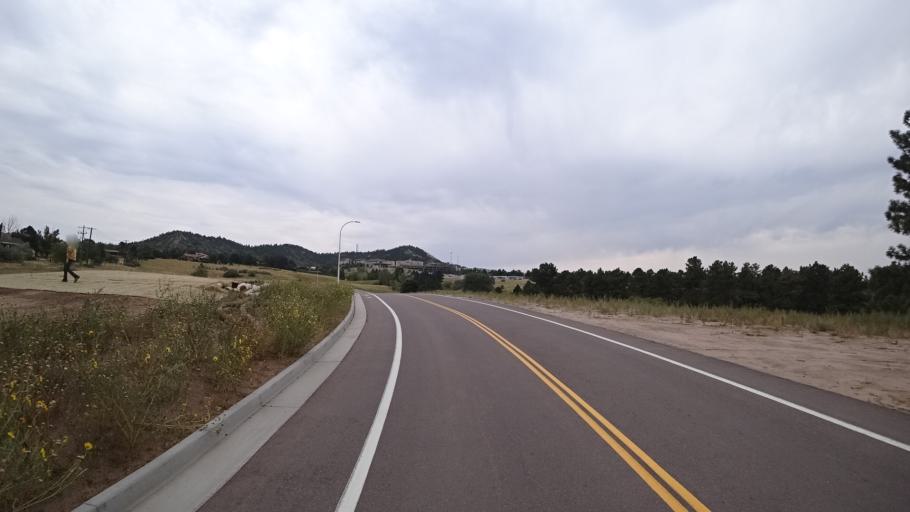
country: US
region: Colorado
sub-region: El Paso County
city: Colorado Springs
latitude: 38.9020
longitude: -104.8143
